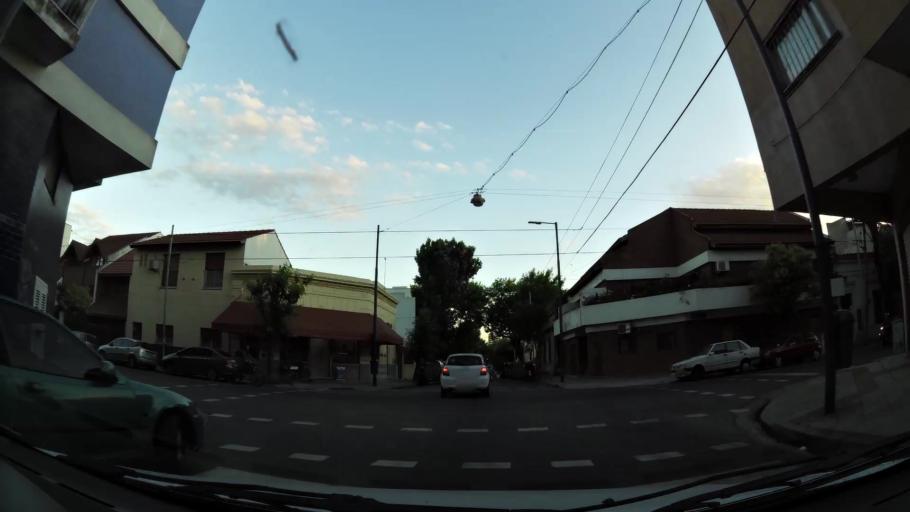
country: AR
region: Buenos Aires
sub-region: Partido de Vicente Lopez
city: Olivos
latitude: -34.5450
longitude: -58.4788
